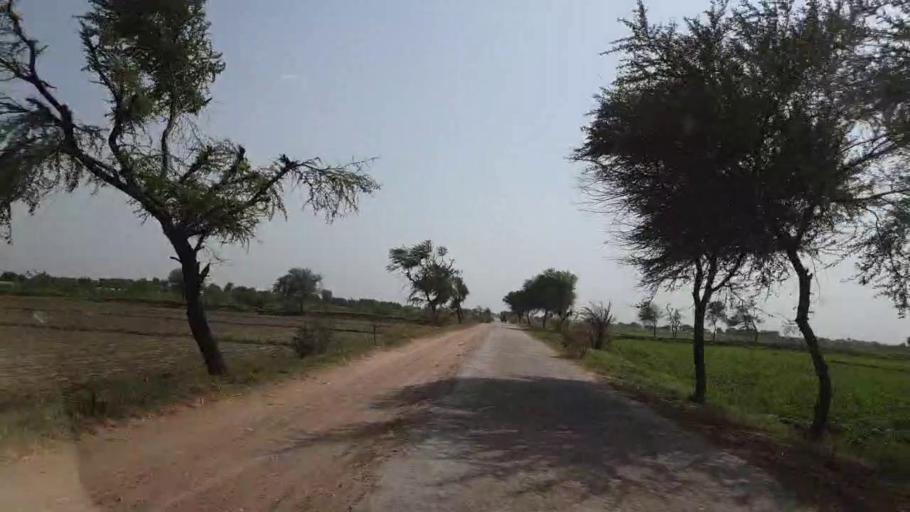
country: PK
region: Sindh
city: Rajo Khanani
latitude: 25.0280
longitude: 68.8730
